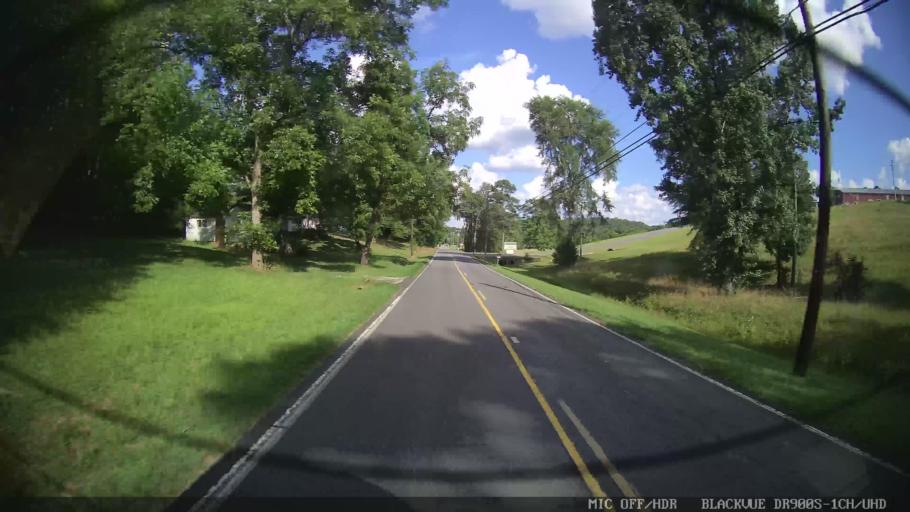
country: US
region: Georgia
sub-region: Floyd County
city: Lindale
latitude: 34.2017
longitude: -85.0913
